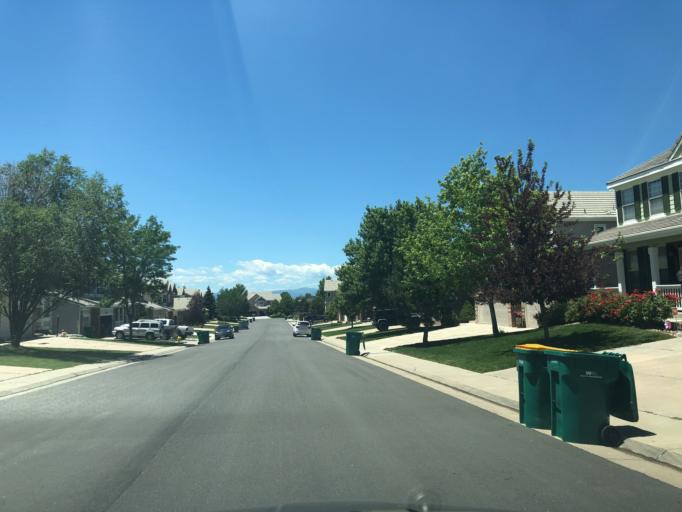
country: US
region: Colorado
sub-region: Arapahoe County
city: Dove Valley
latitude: 39.6082
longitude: -104.7580
